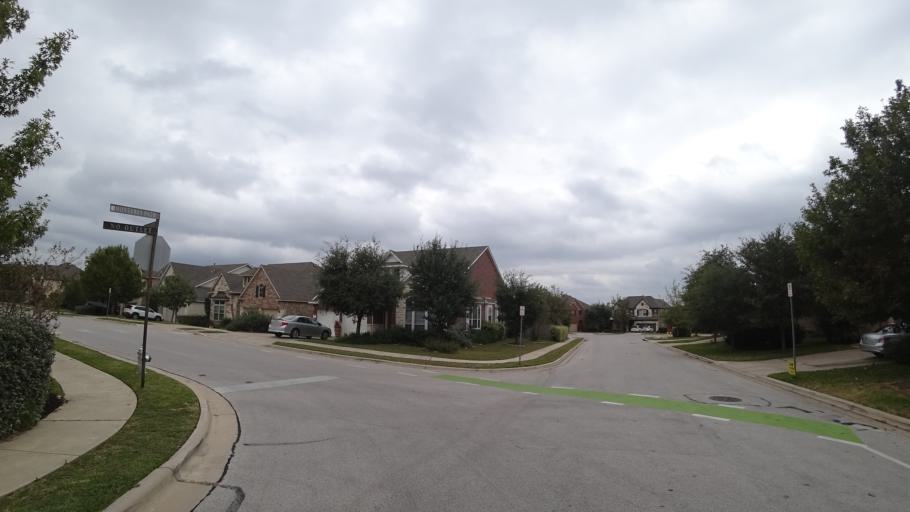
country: US
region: Texas
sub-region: Travis County
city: Bee Cave
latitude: 30.3470
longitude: -97.9142
